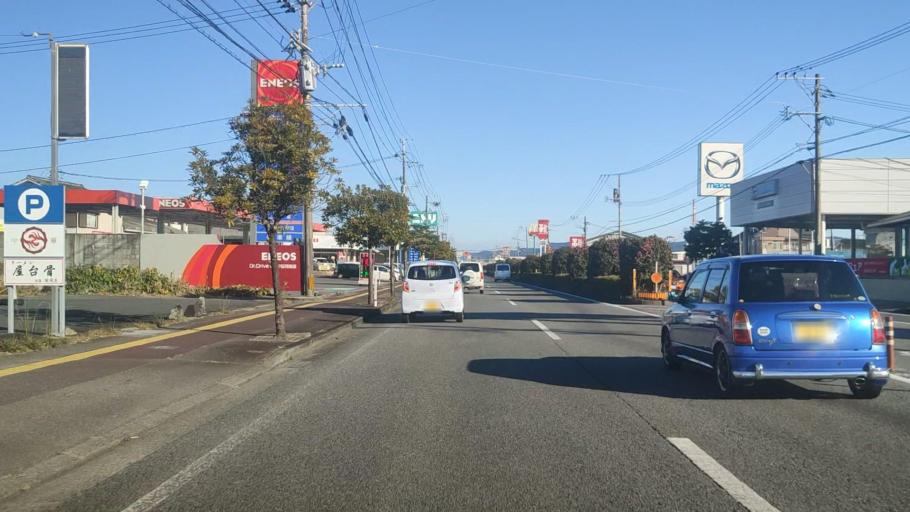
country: JP
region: Miyazaki
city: Nobeoka
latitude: 32.5551
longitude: 131.6794
